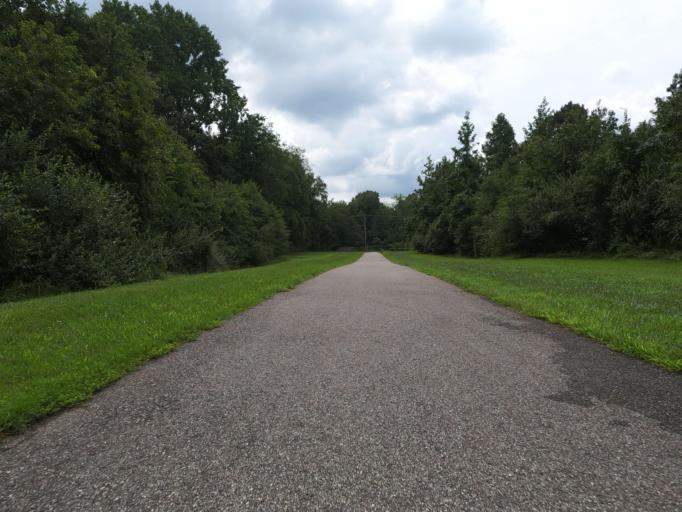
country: US
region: Maryland
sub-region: Anne Arundel County
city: Crofton
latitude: 39.0299
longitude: -76.7243
